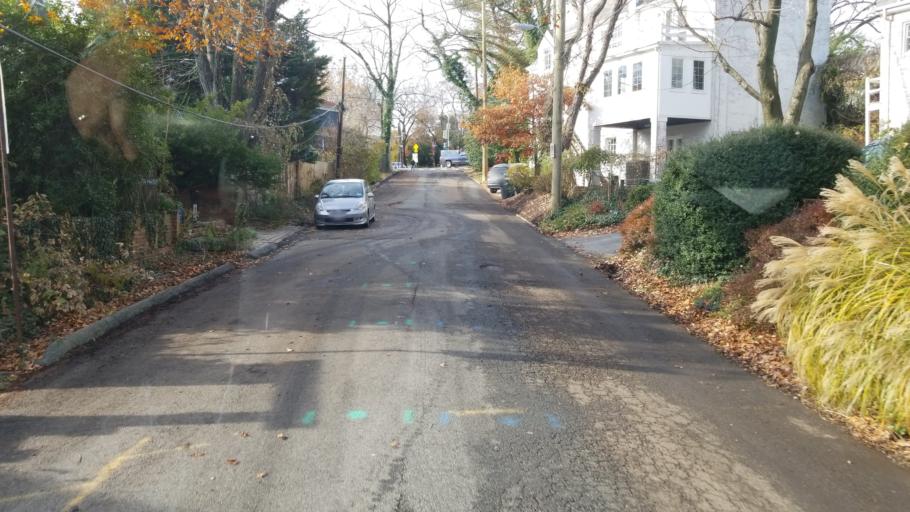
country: US
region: Maryland
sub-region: Montgomery County
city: Friendship Village
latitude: 38.9485
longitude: -77.0761
